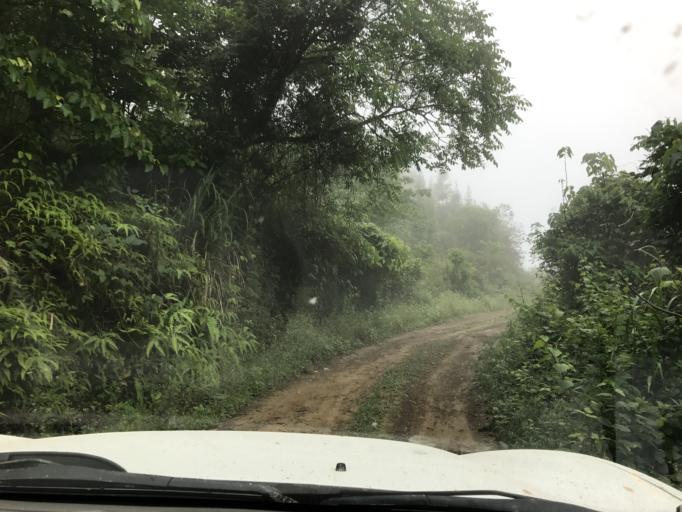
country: CN
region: Guangxi Zhuangzu Zizhiqu
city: Leli
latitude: 24.8117
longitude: 106.0780
